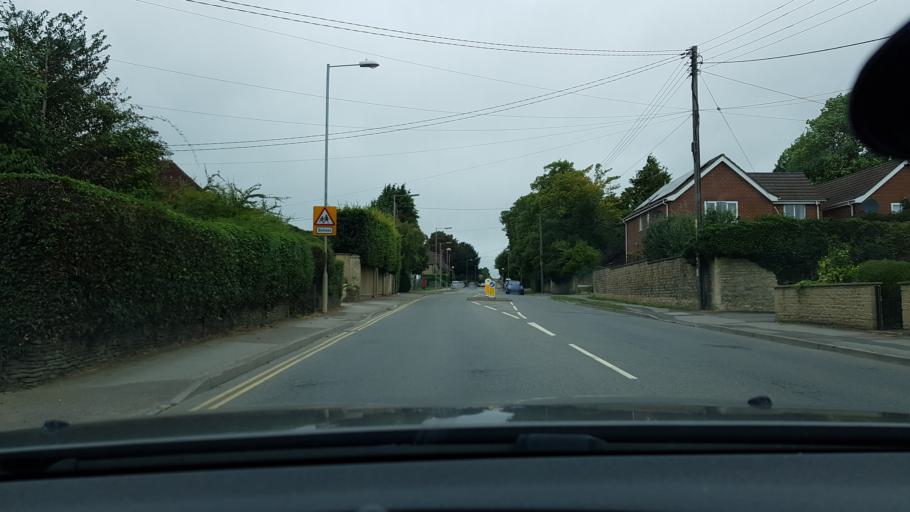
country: GB
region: England
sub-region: Wiltshire
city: Calne
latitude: 51.4289
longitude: -1.9958
